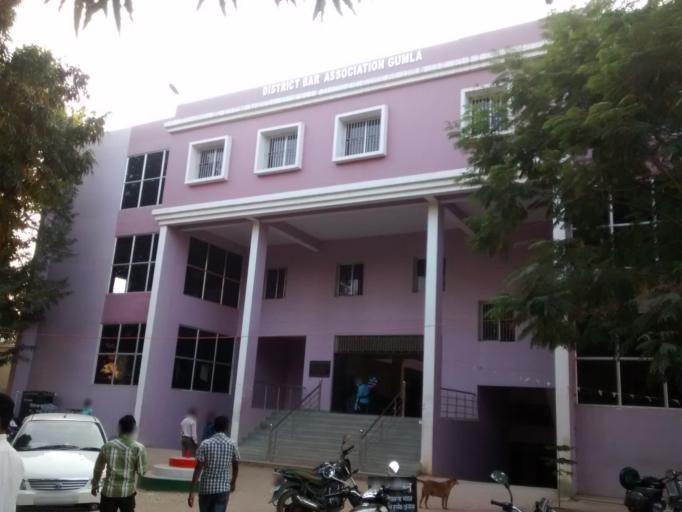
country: IN
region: Chhattisgarh
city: Gumla
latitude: 23.0377
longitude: 84.5373
